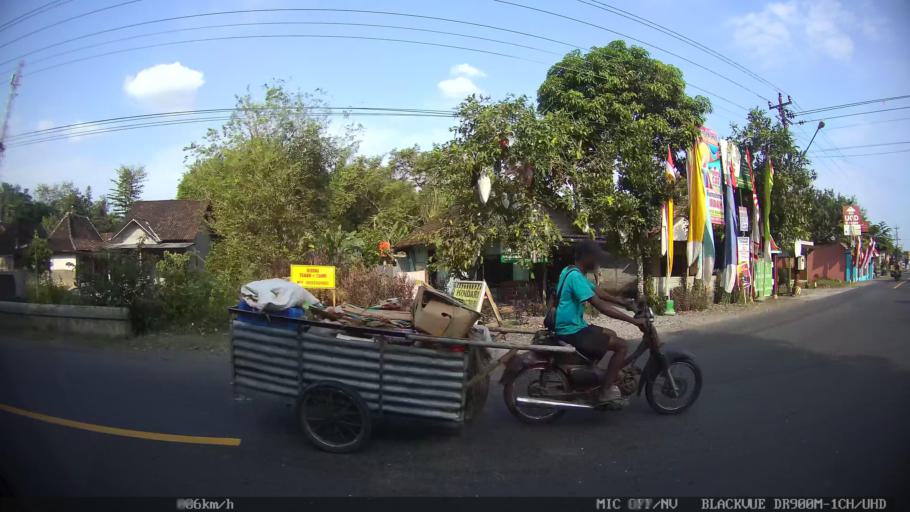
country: ID
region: Central Java
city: Candi Prambanan
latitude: -7.7285
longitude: 110.4721
